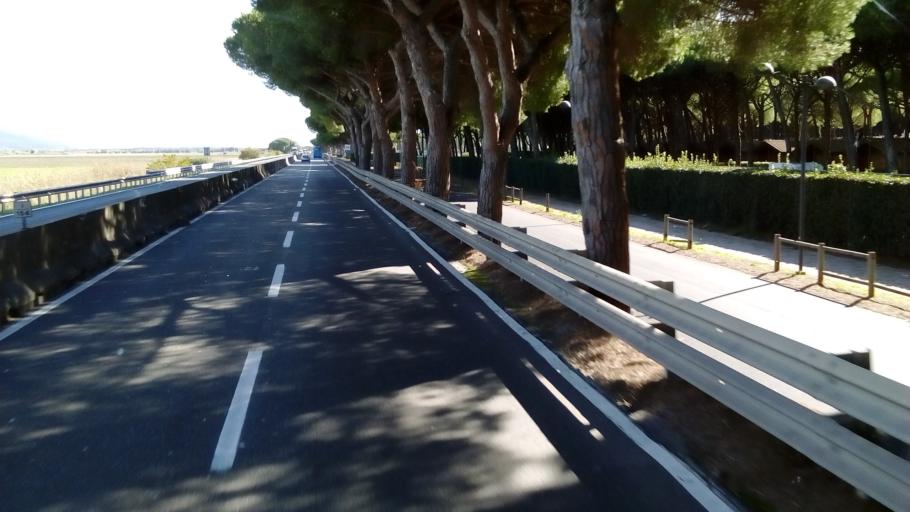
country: IT
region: Tuscany
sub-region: Provincia di Grosseto
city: Fonteblanda
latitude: 42.5319
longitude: 11.1865
